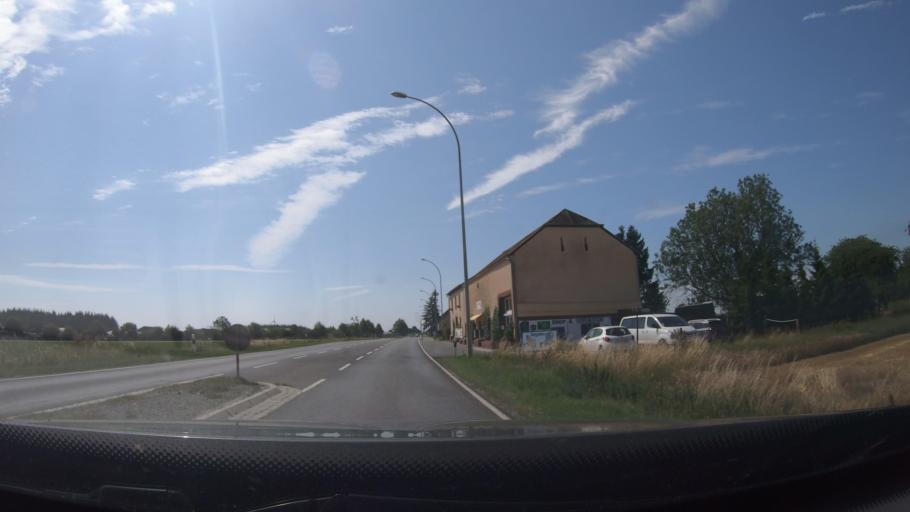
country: LU
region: Diekirch
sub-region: Canton de Clervaux
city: Hosingen
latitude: 50.0004
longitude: 6.0855
